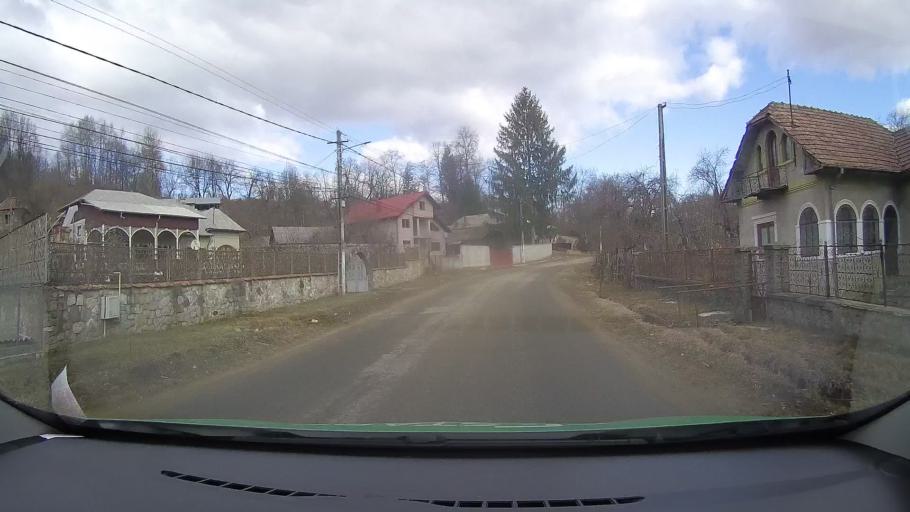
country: RO
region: Dambovita
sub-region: Comuna Buciumeni
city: Buciumeni
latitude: 45.1288
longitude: 25.4671
